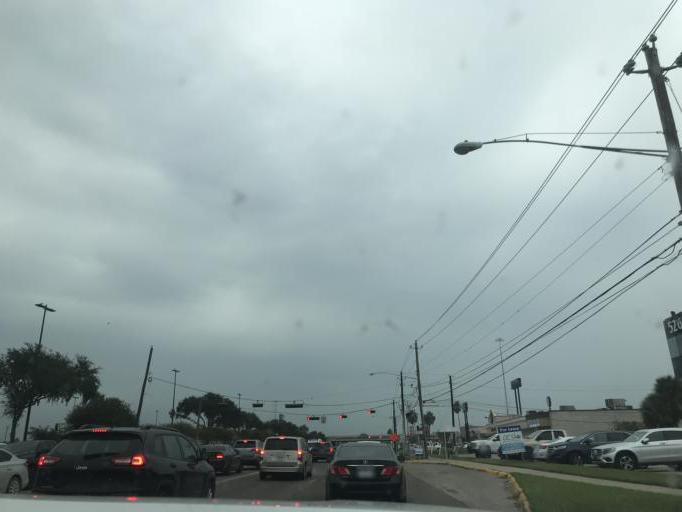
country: US
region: Texas
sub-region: Nueces County
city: Corpus Christi
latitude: 27.7053
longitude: -97.3714
